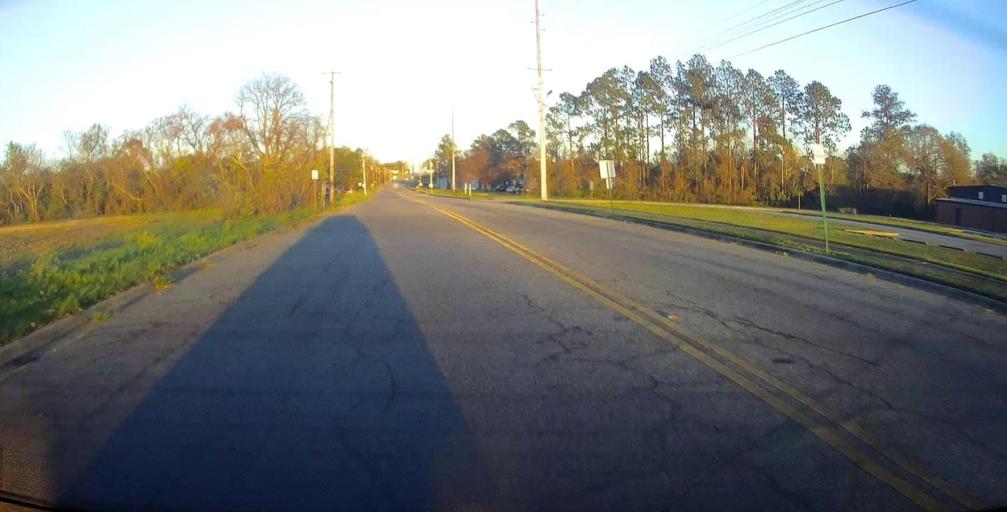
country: US
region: Georgia
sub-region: Crisp County
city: Cordele
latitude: 31.9552
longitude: -83.7960
